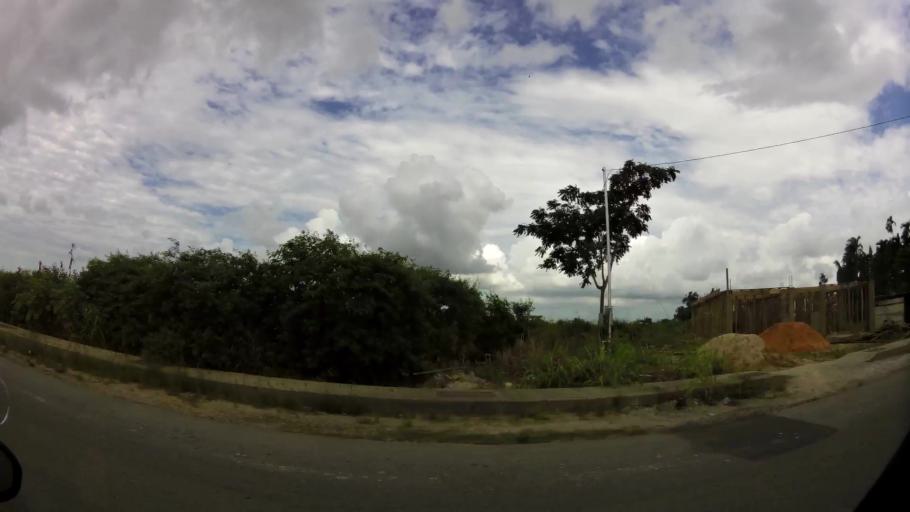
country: TT
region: Couva-Tabaquite-Talparo
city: Couva
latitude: 10.4586
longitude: -61.4291
